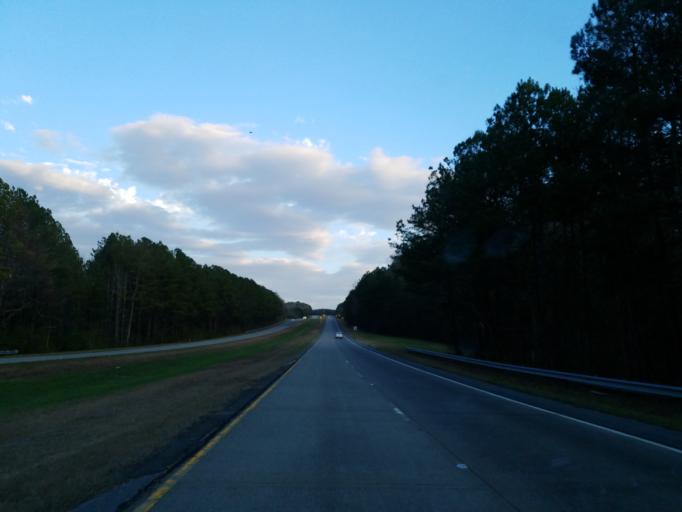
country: US
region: Georgia
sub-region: Pickens County
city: Nelson
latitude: 34.3789
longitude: -84.3881
